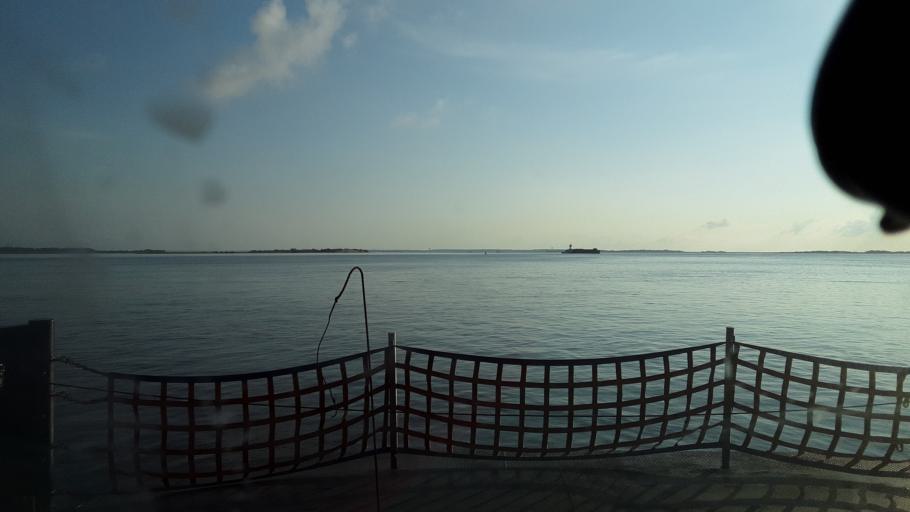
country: US
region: North Carolina
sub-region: Brunswick County
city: Southport
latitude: 33.9409
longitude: -77.9771
